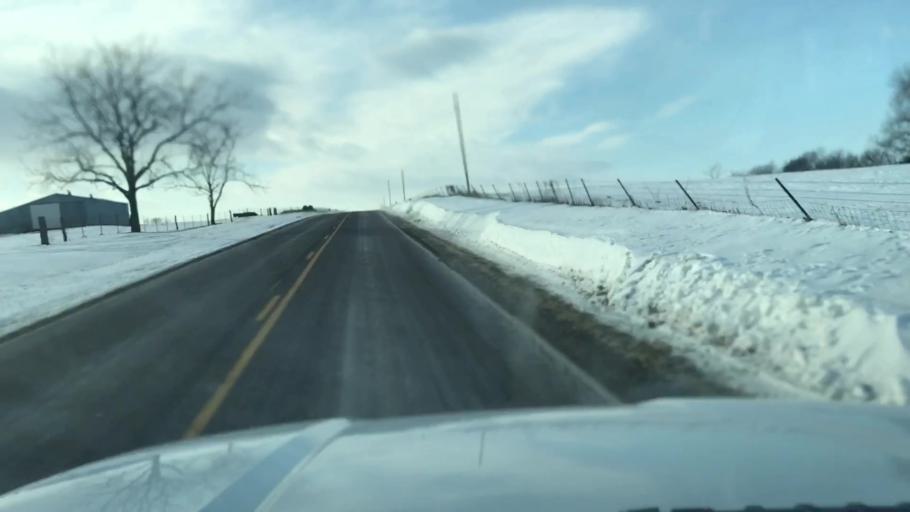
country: US
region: Missouri
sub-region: Nodaway County
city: Maryville
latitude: 40.2008
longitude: -94.8993
